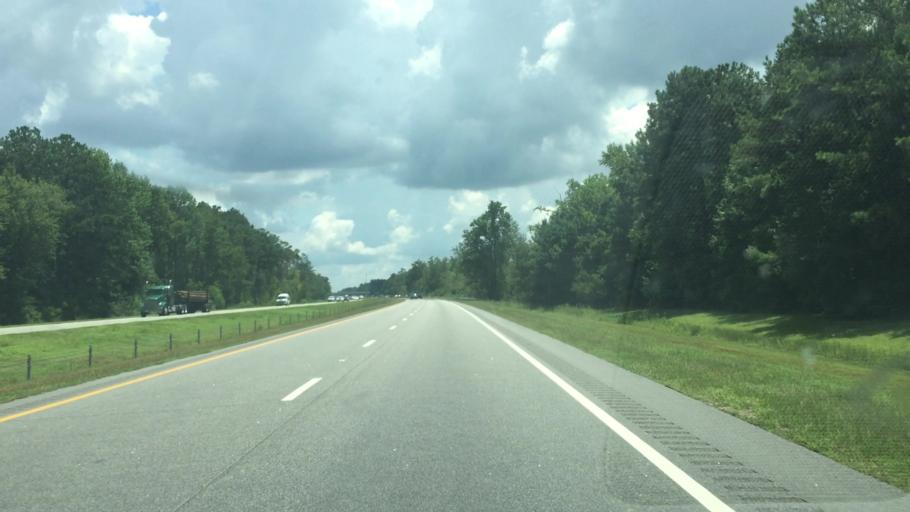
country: US
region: North Carolina
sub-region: Columbus County
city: Chadbourn
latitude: 34.4032
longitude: -78.9184
